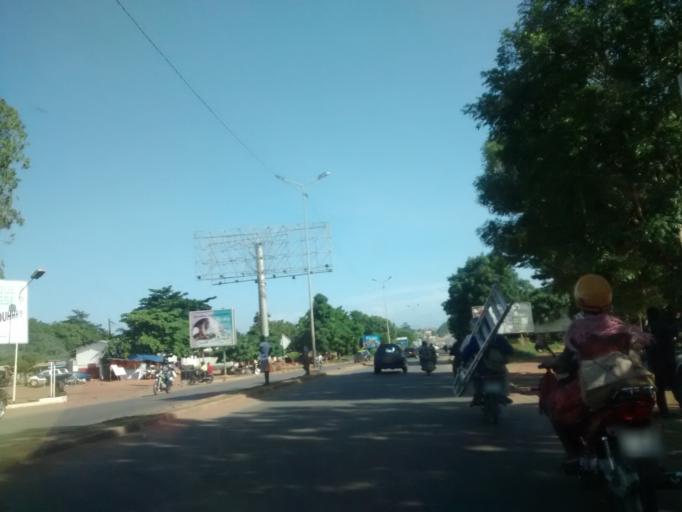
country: TG
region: Maritime
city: Lome
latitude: 6.1655
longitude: 1.2020
